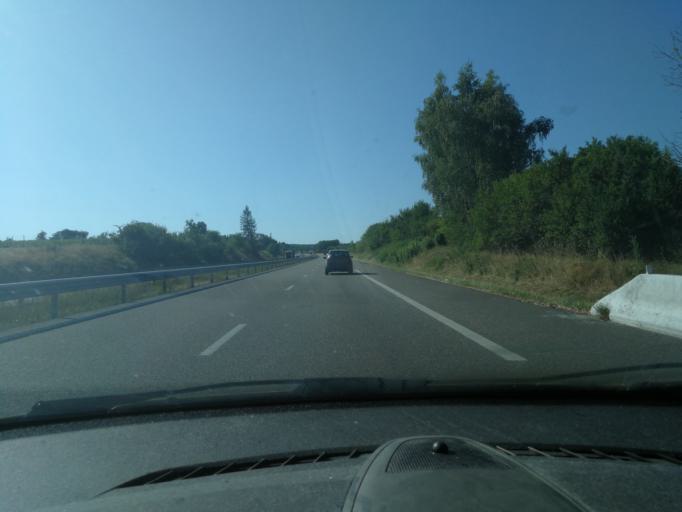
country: FR
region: Alsace
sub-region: Departement du Bas-Rhin
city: Sarre-Union
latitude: 48.9475
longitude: 7.0977
